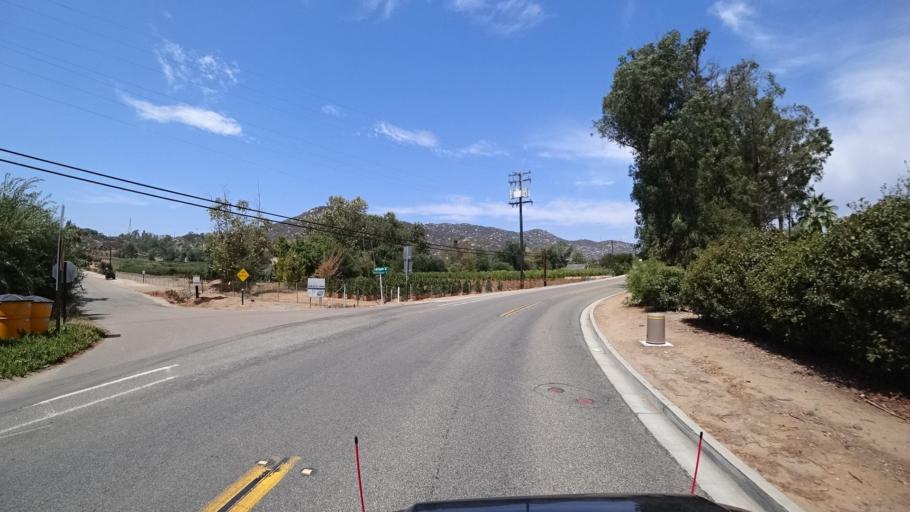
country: US
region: California
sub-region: San Diego County
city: Hidden Meadows
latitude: 33.1818
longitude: -117.0925
